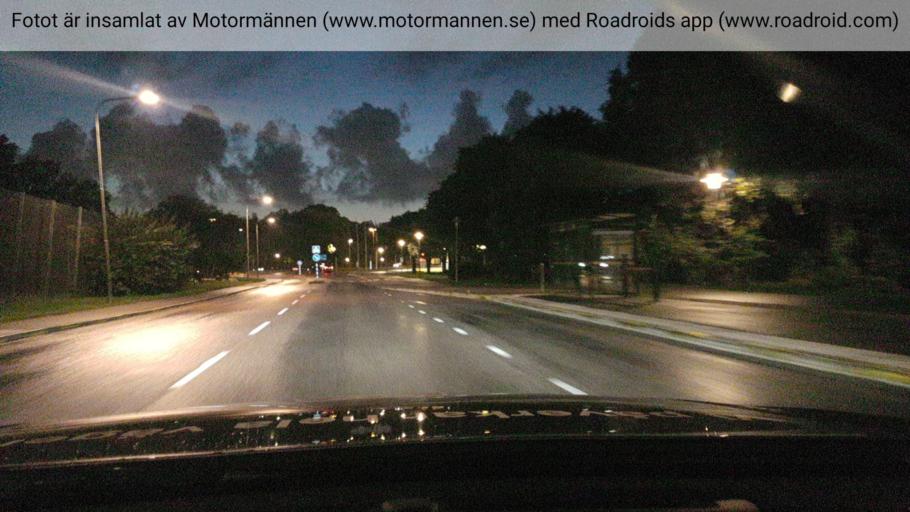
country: SE
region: Stockholm
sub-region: Huddinge Kommun
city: Huddinge
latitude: 59.2561
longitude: 18.0177
